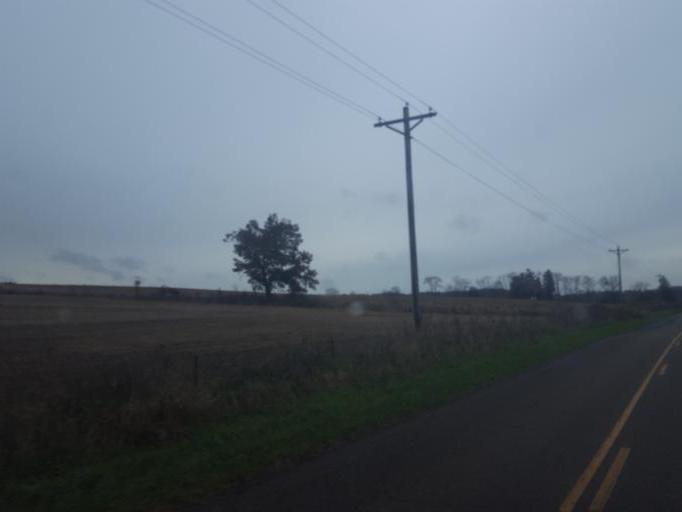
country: US
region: Ohio
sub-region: Knox County
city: Gambier
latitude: 40.4706
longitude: -82.3966
